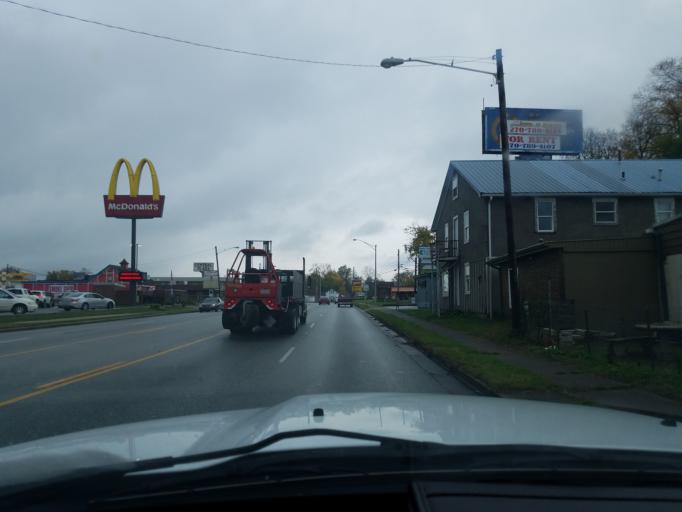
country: US
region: Kentucky
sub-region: Taylor County
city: Campbellsville
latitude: 37.3441
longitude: -85.3403
